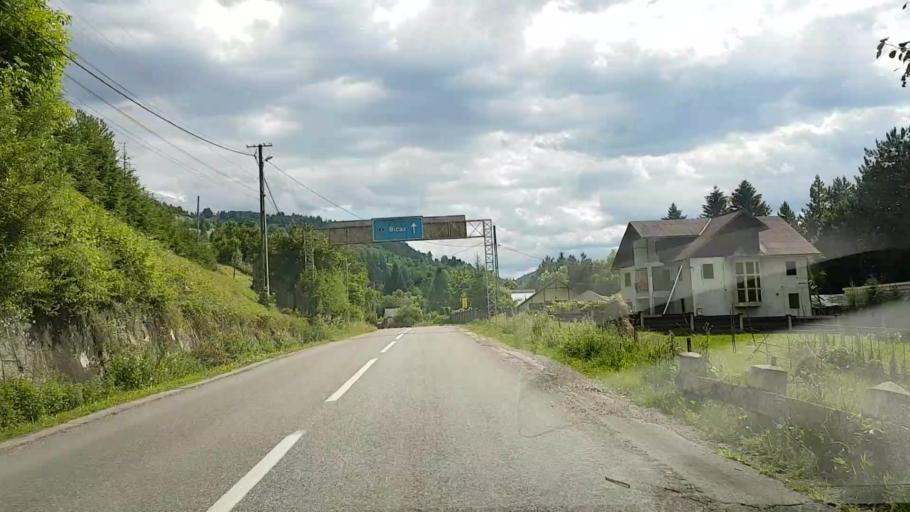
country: RO
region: Neamt
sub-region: Comuna Poiana Teiului
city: Poiana Teiului
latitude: 47.0859
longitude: 25.9703
